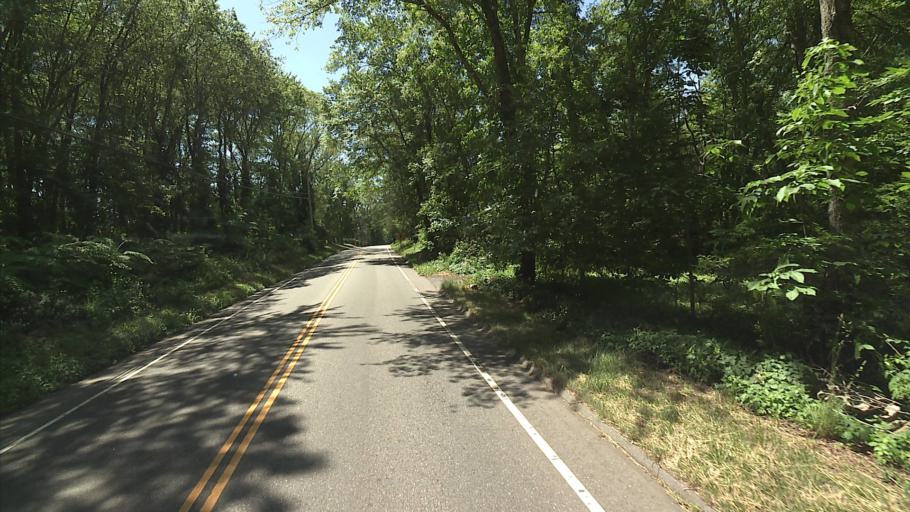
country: US
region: Rhode Island
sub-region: Washington County
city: Hopkinton
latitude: 41.4720
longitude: -71.8323
